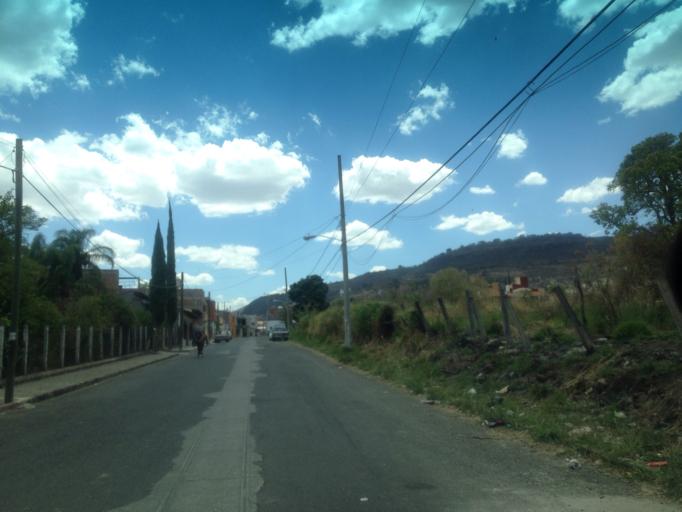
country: MX
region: Jalisco
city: Atotonilco el Alto
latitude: 20.5531
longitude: -102.5019
